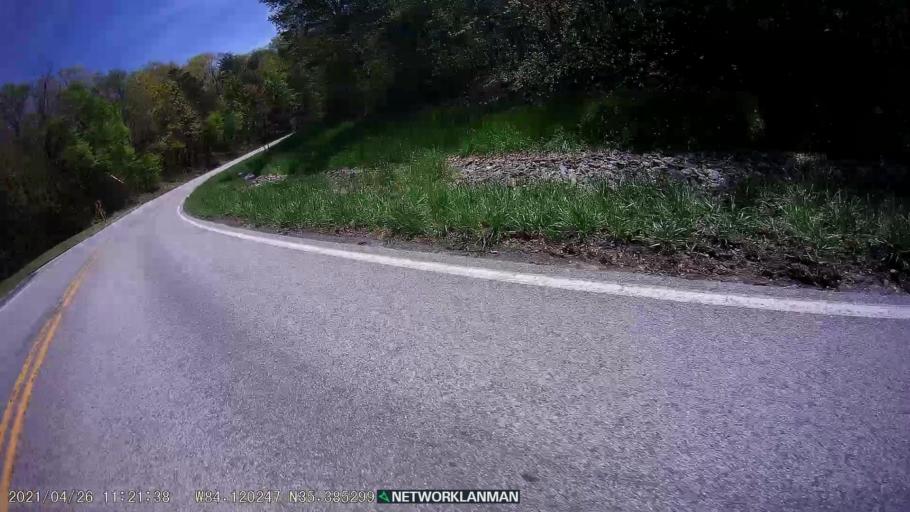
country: US
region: Tennessee
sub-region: Monroe County
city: Vonore
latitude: 35.3853
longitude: -84.1201
